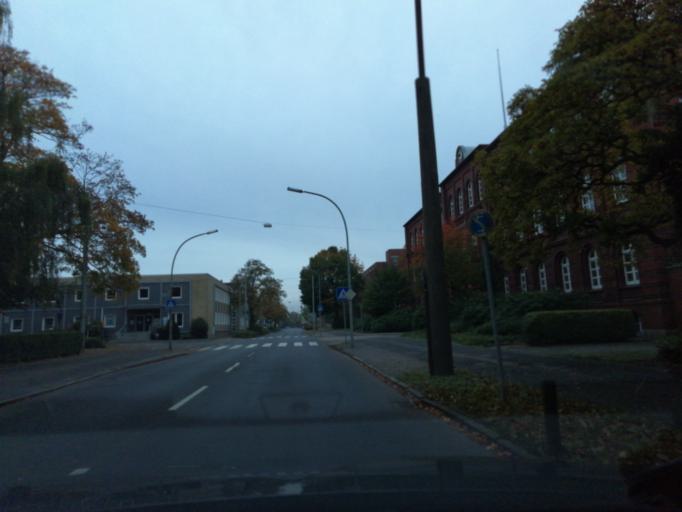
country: DE
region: Lower Saxony
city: Wilhelmshaven
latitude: 53.5191
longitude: 8.1237
